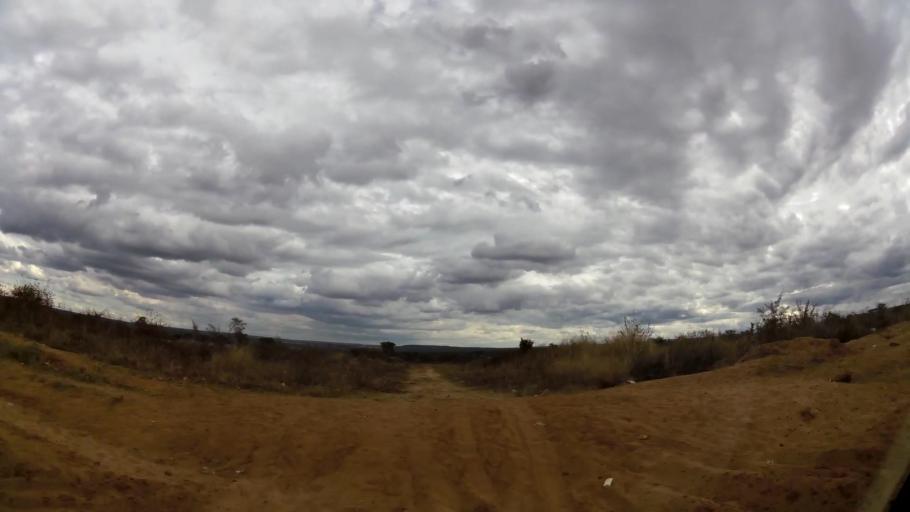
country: ZA
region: Limpopo
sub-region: Waterberg District Municipality
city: Modimolle
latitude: -24.6933
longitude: 28.4224
